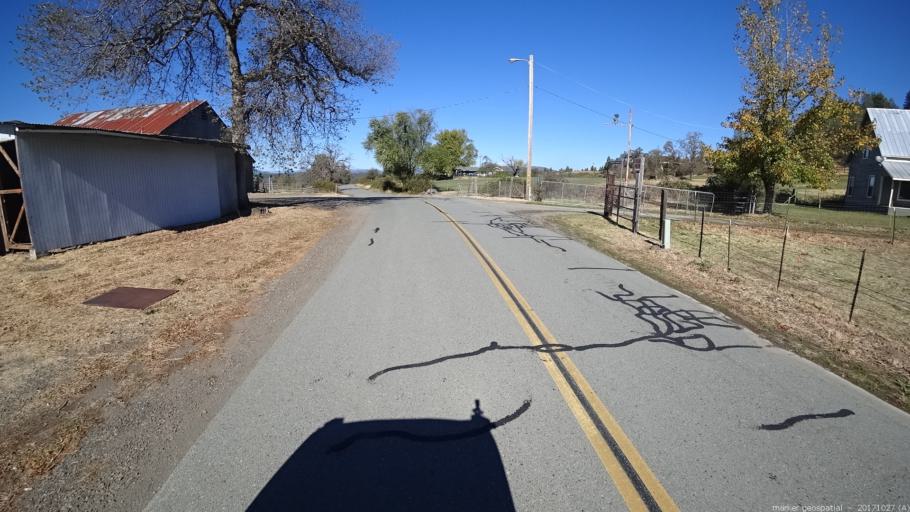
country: US
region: California
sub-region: Shasta County
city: Shingletown
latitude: 40.7595
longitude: -121.9676
